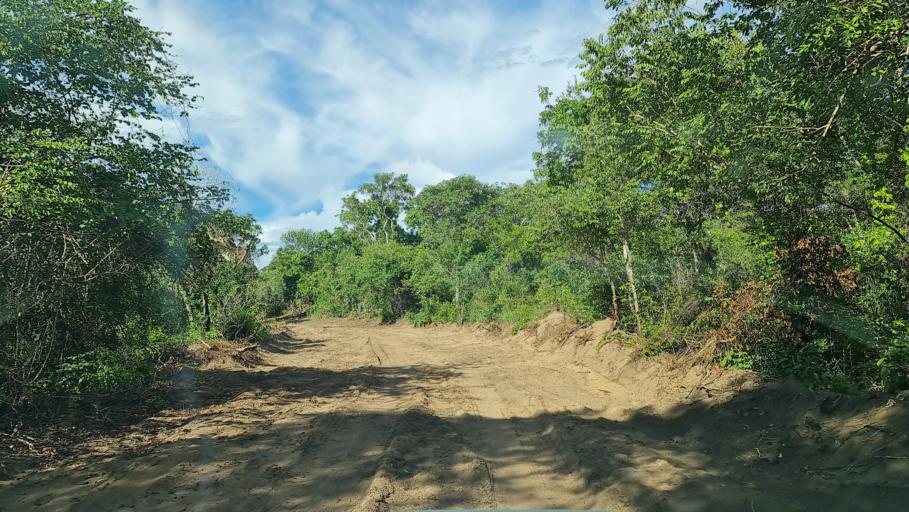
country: MZ
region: Nampula
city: Antonio Enes
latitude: -15.5317
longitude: 40.1254
